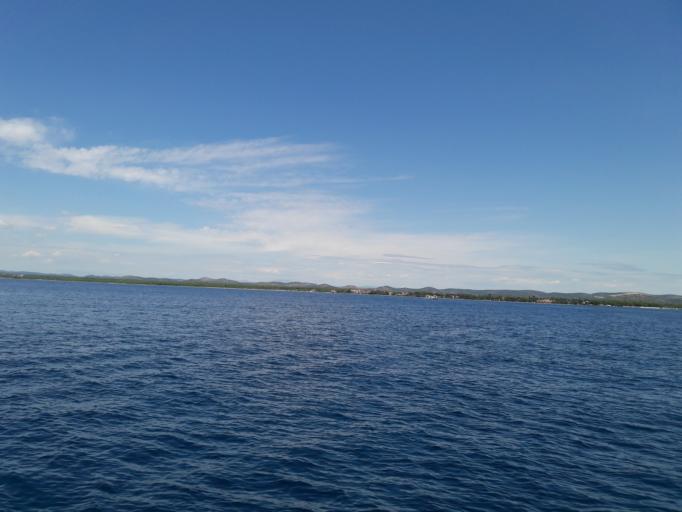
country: HR
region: Sibensko-Kniniska
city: Vodice
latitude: 43.7113
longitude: 15.8339
